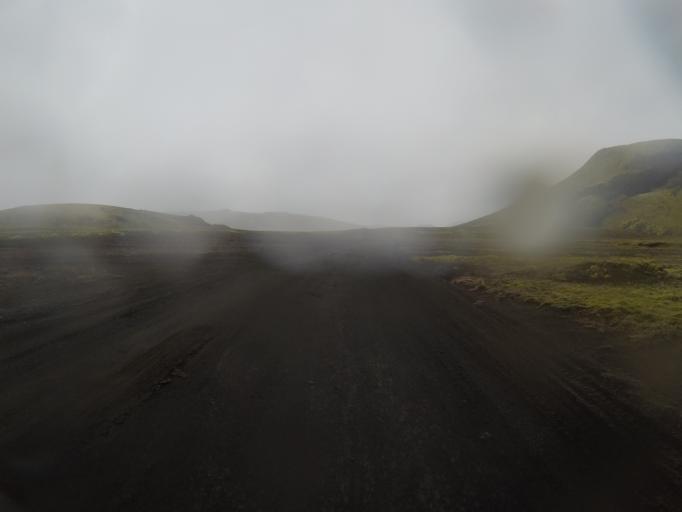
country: IS
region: South
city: Vestmannaeyjar
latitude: 63.9714
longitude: -18.8280
